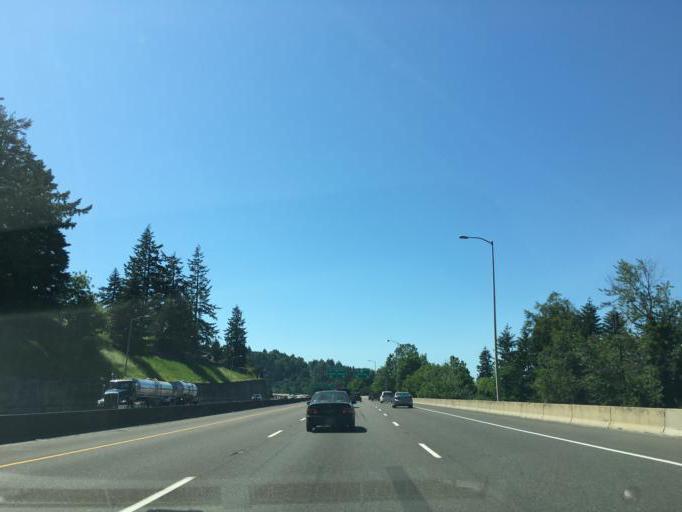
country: US
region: Oregon
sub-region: Multnomah County
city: Lents
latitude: 45.5473
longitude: -122.5439
